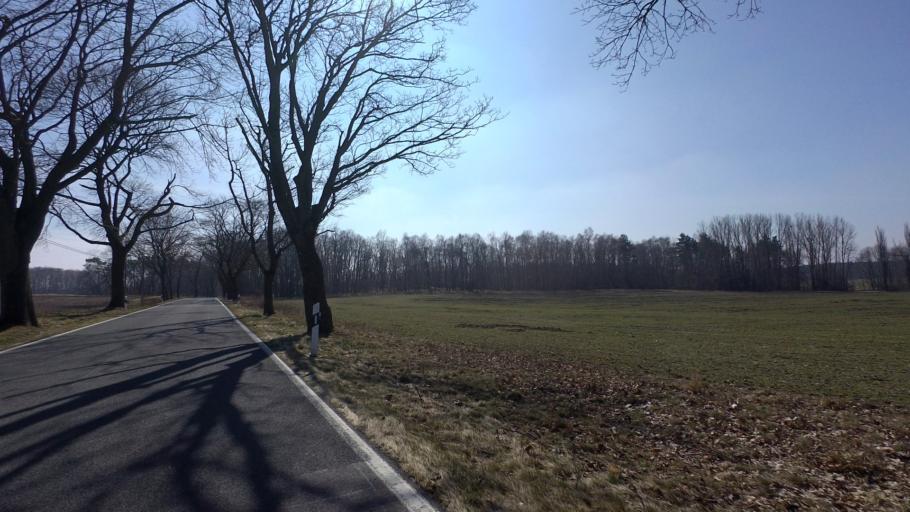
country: DE
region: Brandenburg
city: Wiesenburg
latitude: 52.0260
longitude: 12.5278
